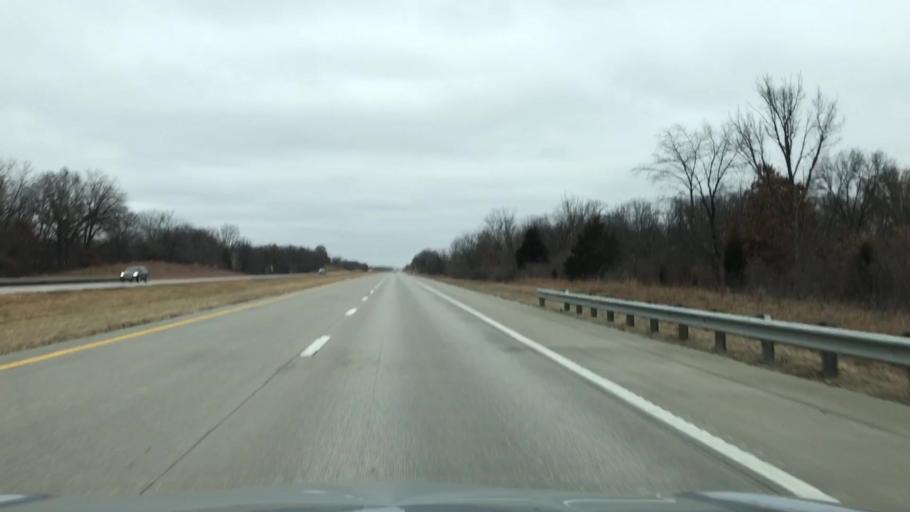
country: US
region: Missouri
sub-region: Clay County
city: Kearney
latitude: 39.3958
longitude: -94.3568
